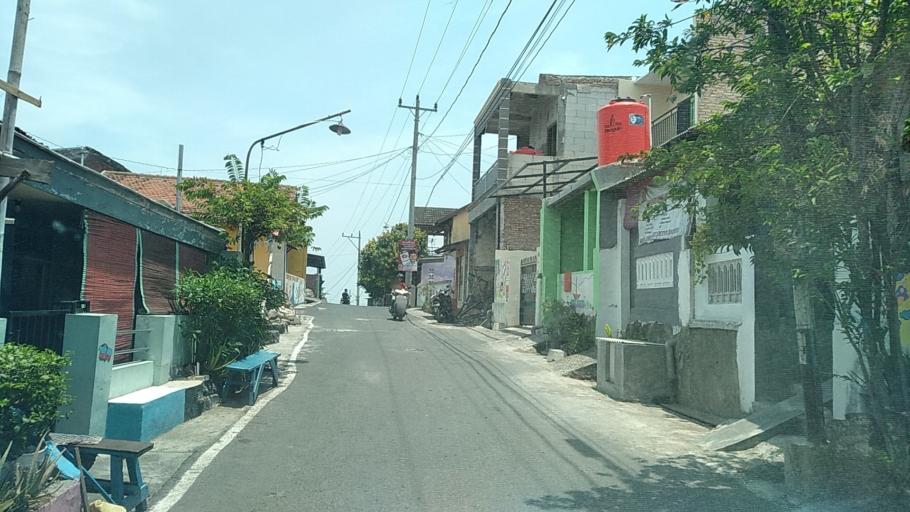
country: ID
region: Central Java
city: Semarang
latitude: -7.0108
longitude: 110.4499
